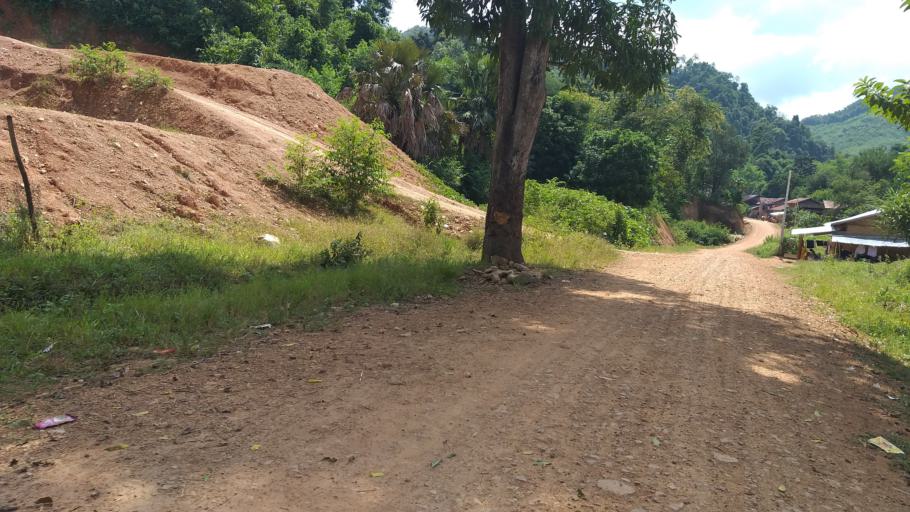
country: LA
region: Phongsali
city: Khoa
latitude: 21.3217
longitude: 102.5685
